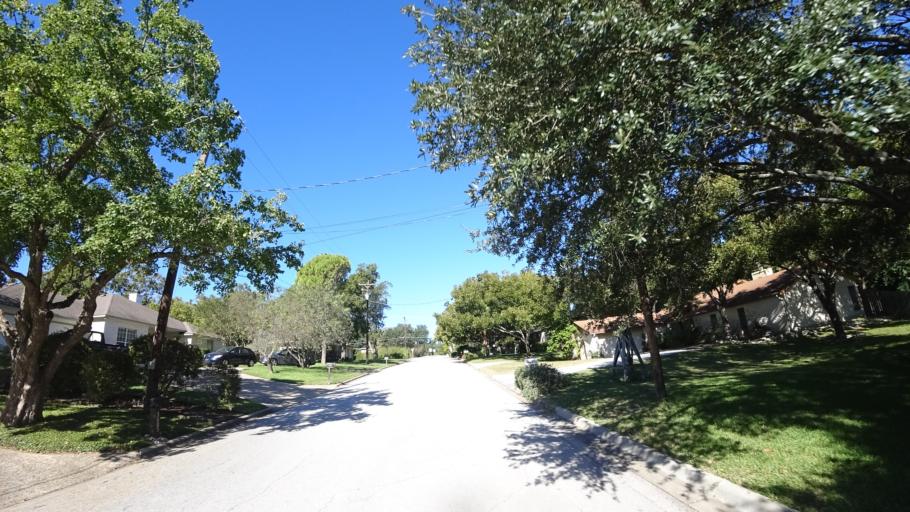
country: US
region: Texas
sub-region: Travis County
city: Manor
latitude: 30.3330
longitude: -97.6520
